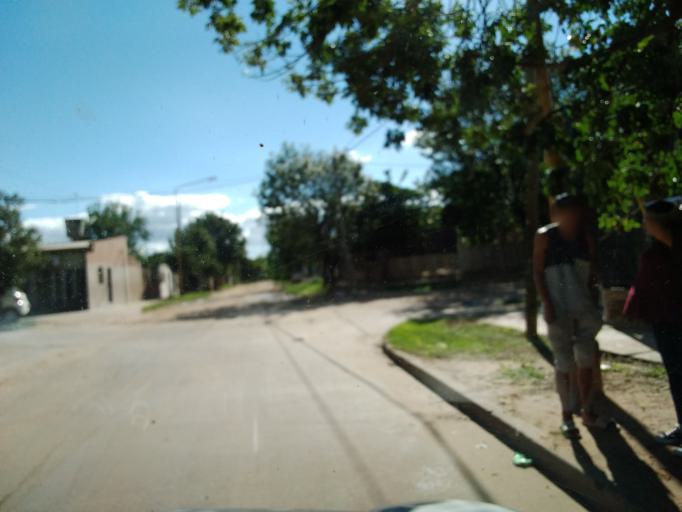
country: AR
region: Corrientes
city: Corrientes
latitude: -27.5043
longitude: -58.8045
